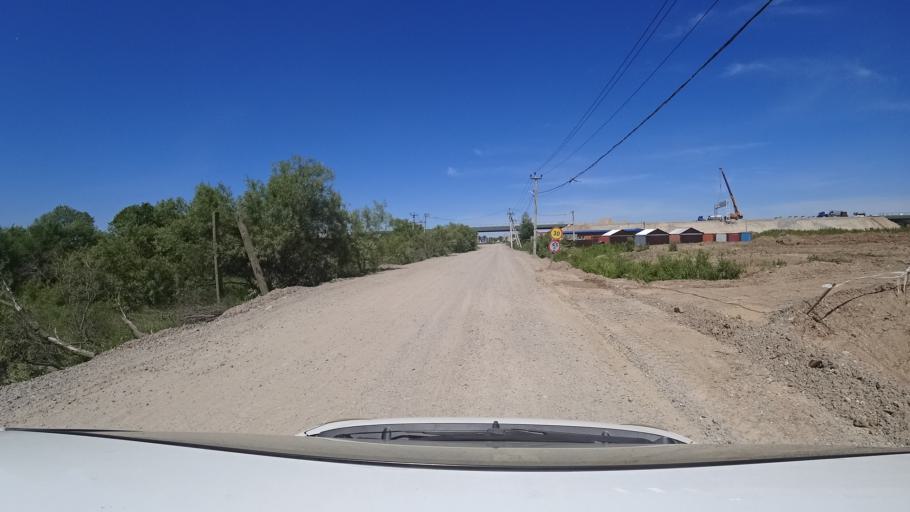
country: RU
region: Khabarovsk Krai
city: Topolevo
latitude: 48.4801
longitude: 135.1736
